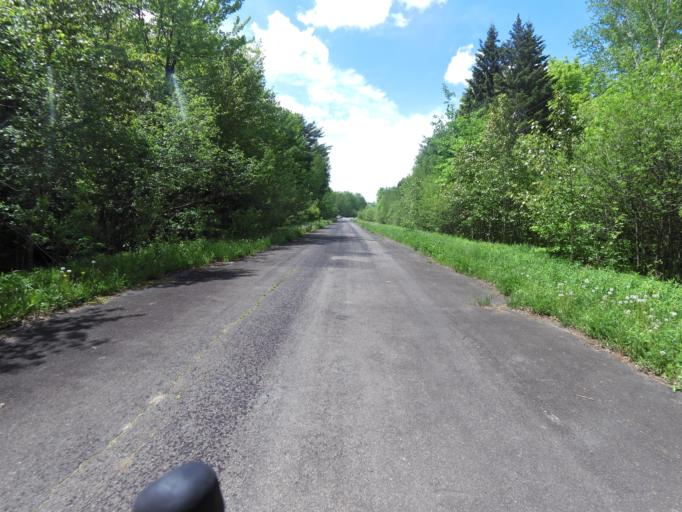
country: CA
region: Ontario
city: Ottawa
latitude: 45.4092
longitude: -75.5447
